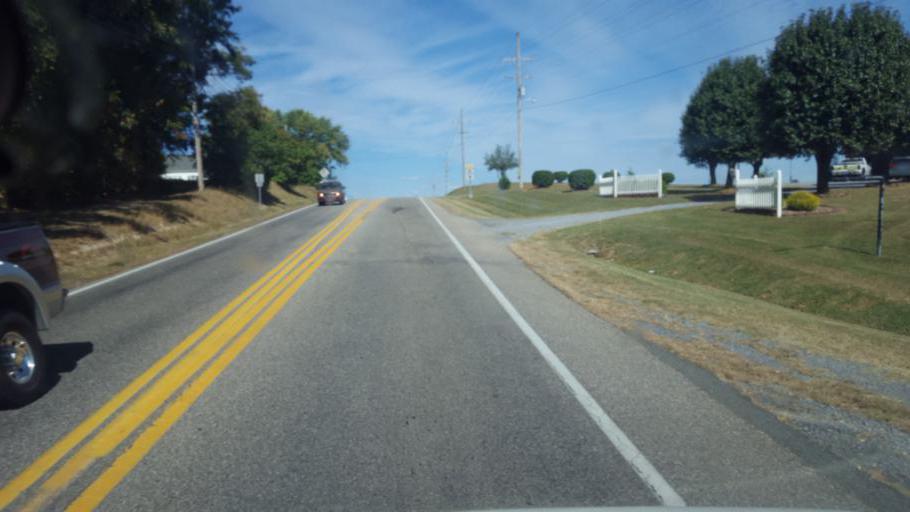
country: US
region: Virginia
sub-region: Page County
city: Shenandoah
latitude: 38.5598
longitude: -78.6054
